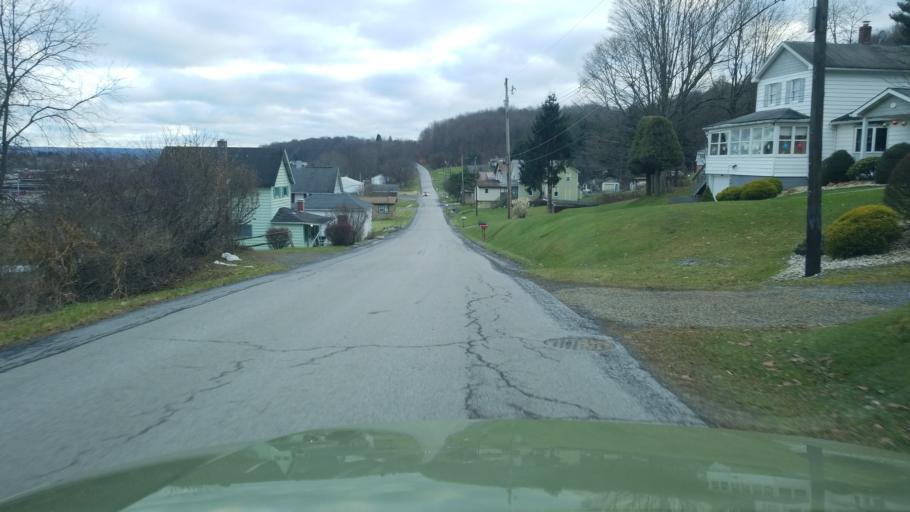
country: US
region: Pennsylvania
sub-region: Jefferson County
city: Falls Creek
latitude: 41.1337
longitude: -78.7856
